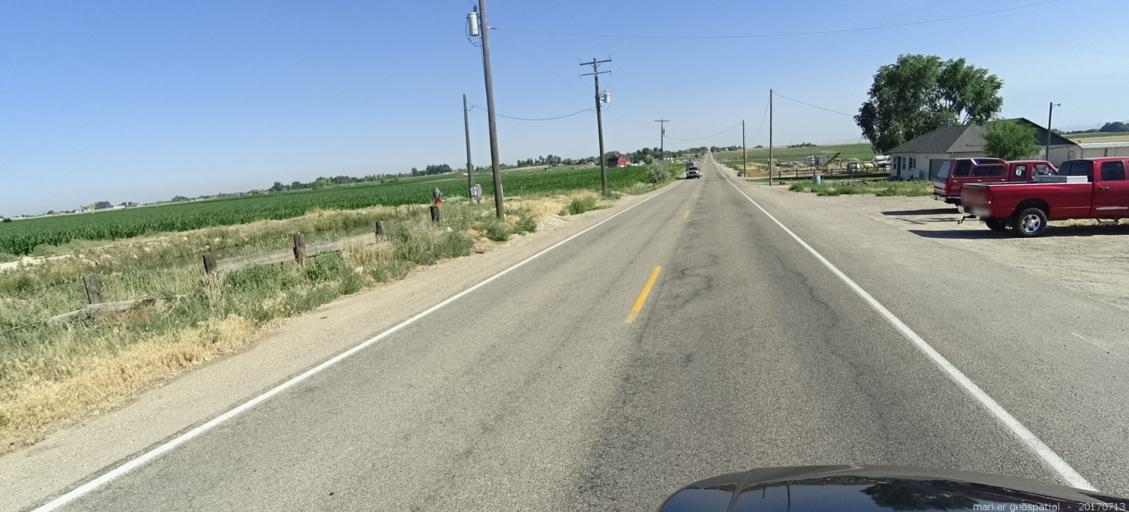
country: US
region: Idaho
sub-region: Ada County
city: Kuna
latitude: 43.5338
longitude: -116.4138
